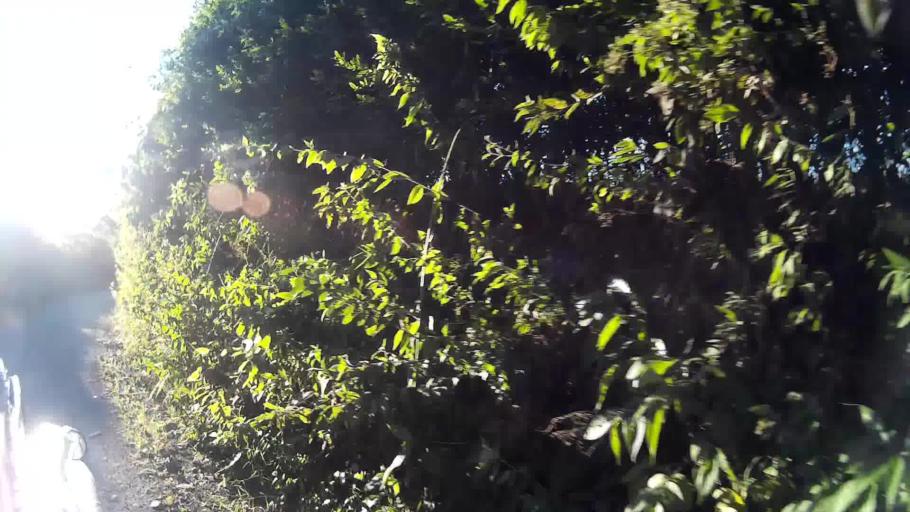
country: CO
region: Valle del Cauca
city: Ulloa
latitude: 4.7330
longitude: -75.6857
